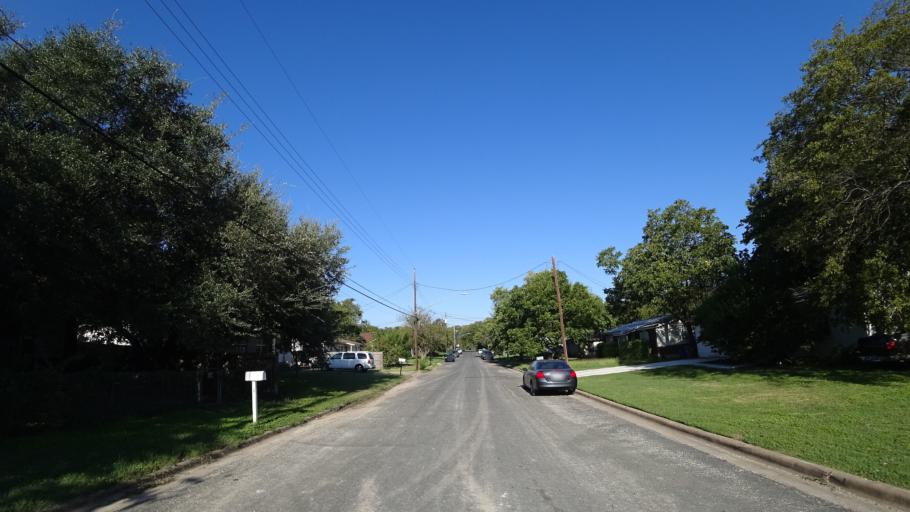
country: US
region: Texas
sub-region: Travis County
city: Austin
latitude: 30.3493
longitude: -97.6997
